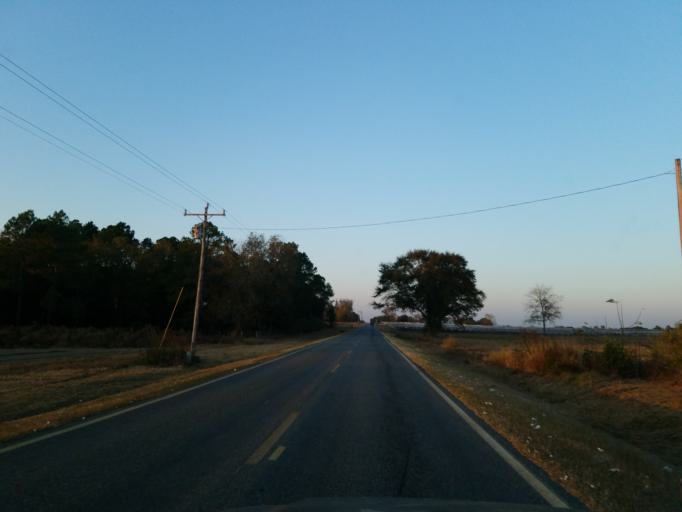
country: US
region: Georgia
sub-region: Ben Hill County
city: Fitzgerald
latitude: 31.6804
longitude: -83.3854
